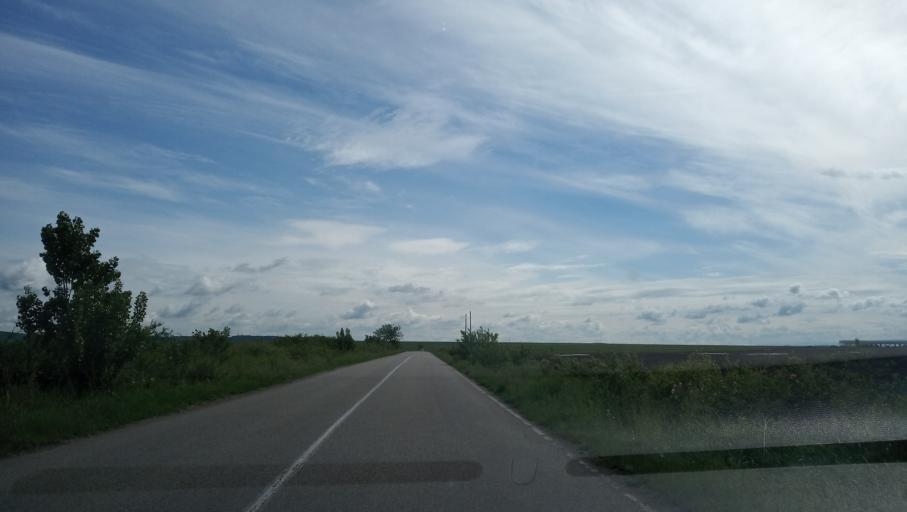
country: RO
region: Timis
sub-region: Comuna Topolovatu Mare
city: Topolovatu Mare
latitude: 45.7858
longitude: 21.6458
